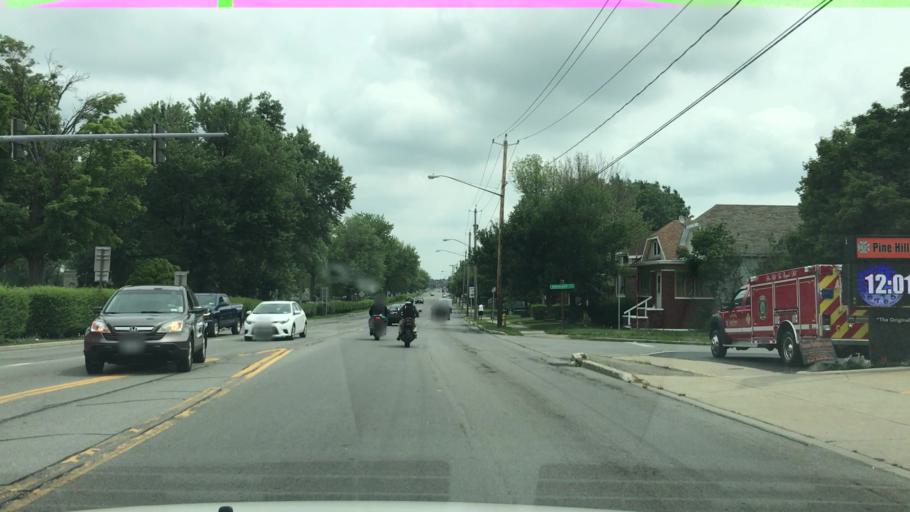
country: US
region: New York
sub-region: Erie County
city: Sloan
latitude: 42.9199
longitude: -78.7931
